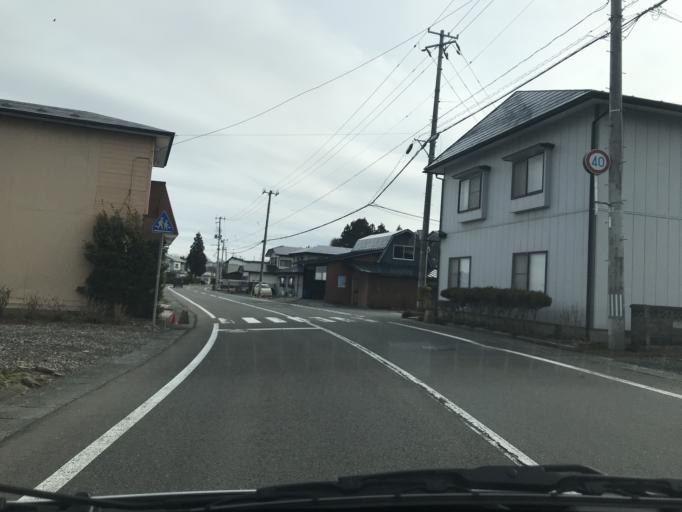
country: JP
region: Iwate
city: Hanamaki
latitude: 39.4245
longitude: 141.0847
